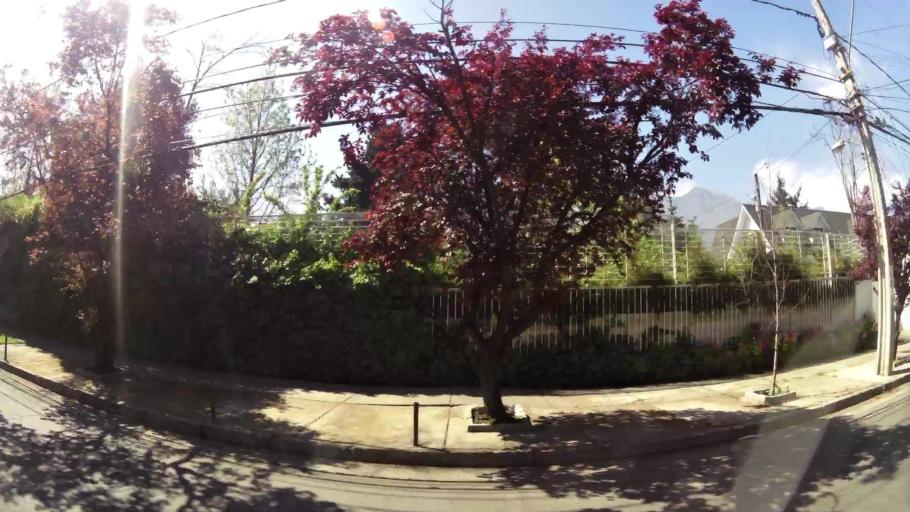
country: CL
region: Santiago Metropolitan
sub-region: Provincia de Santiago
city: Villa Presidente Frei, Nunoa, Santiago, Chile
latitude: -33.4363
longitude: -70.5297
